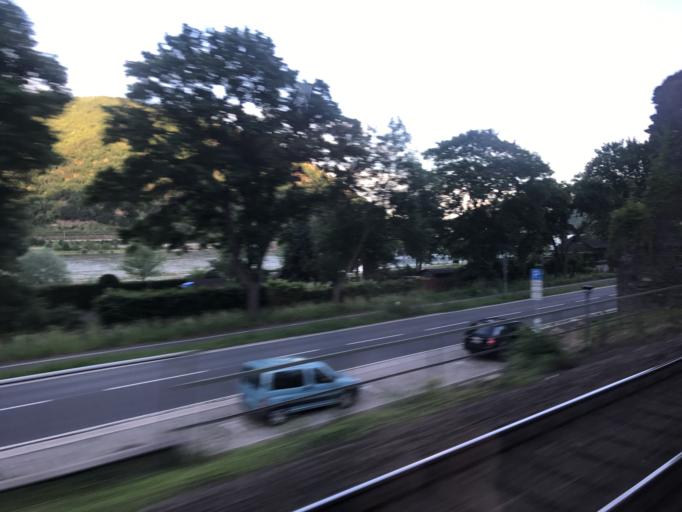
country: DE
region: Rheinland-Pfalz
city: Bacharach
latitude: 50.0620
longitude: 7.7691
